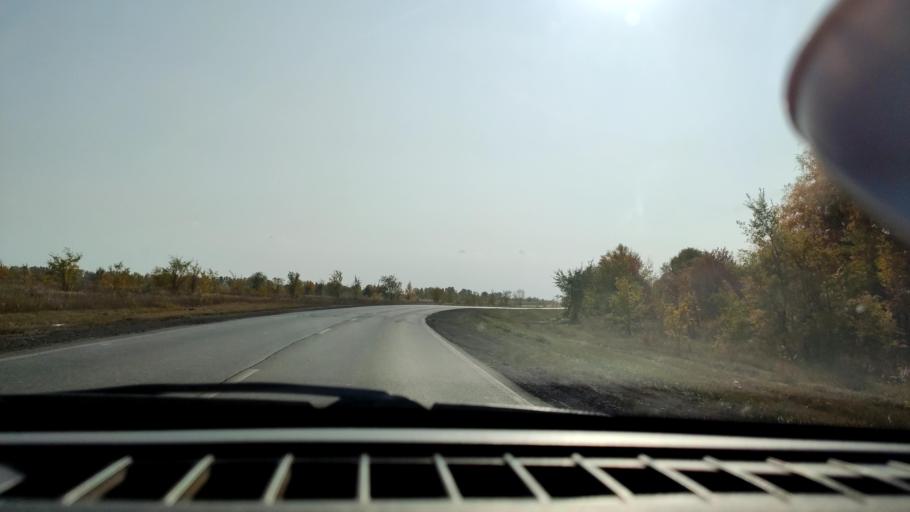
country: RU
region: Samara
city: Smyshlyayevka
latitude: 53.1212
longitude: 50.3670
